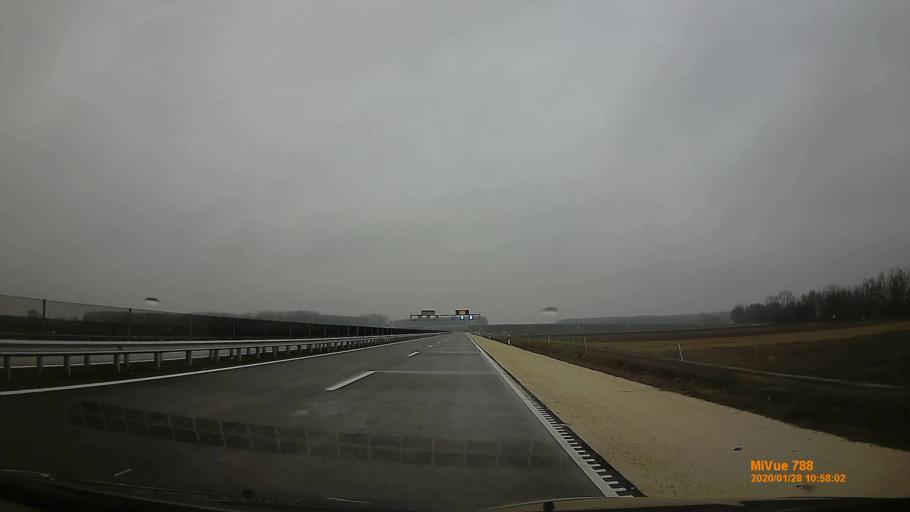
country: HU
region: Pest
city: Peteri
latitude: 47.3747
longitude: 19.4063
